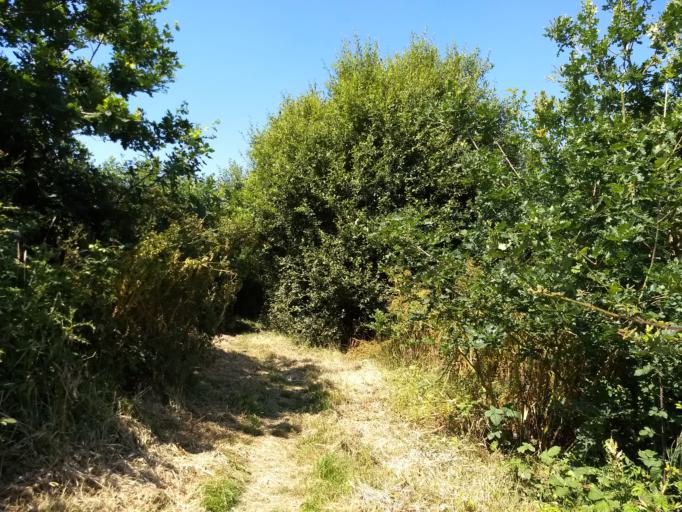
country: GB
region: England
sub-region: Isle of Wight
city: Gurnard
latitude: 50.7330
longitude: -1.3621
